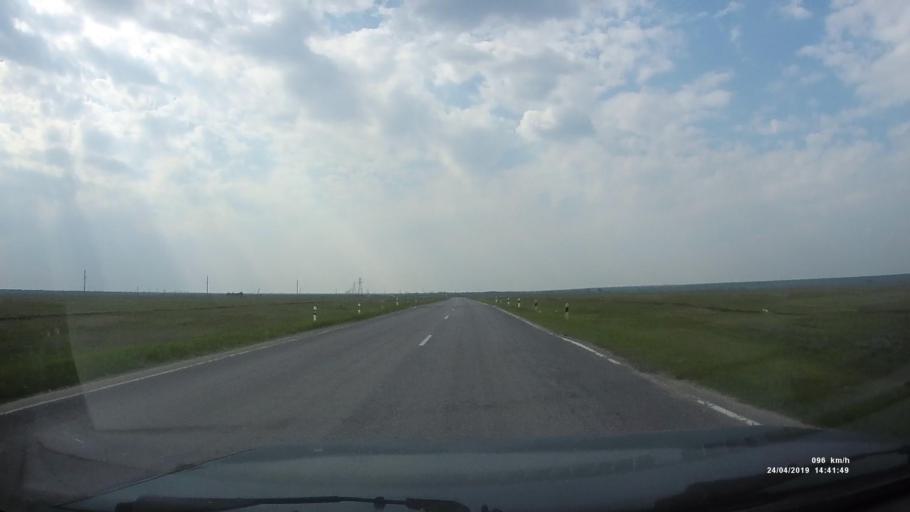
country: RU
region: Rostov
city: Remontnoye
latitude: 46.4483
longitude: 43.8737
